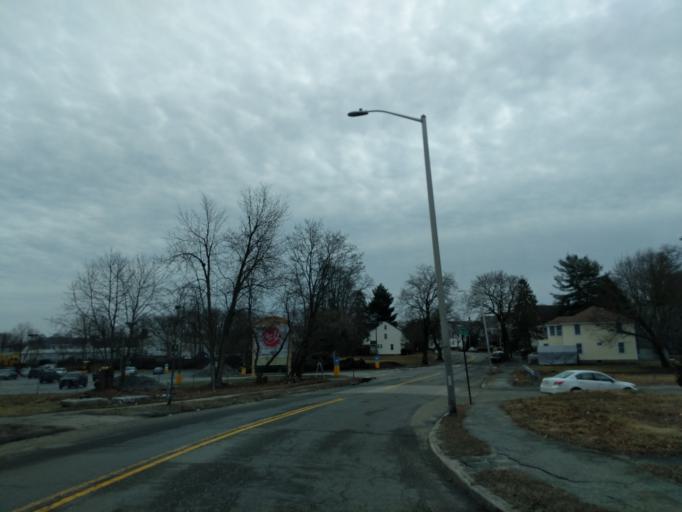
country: US
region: Massachusetts
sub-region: Worcester County
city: Worcester
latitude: 42.2586
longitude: -71.8275
